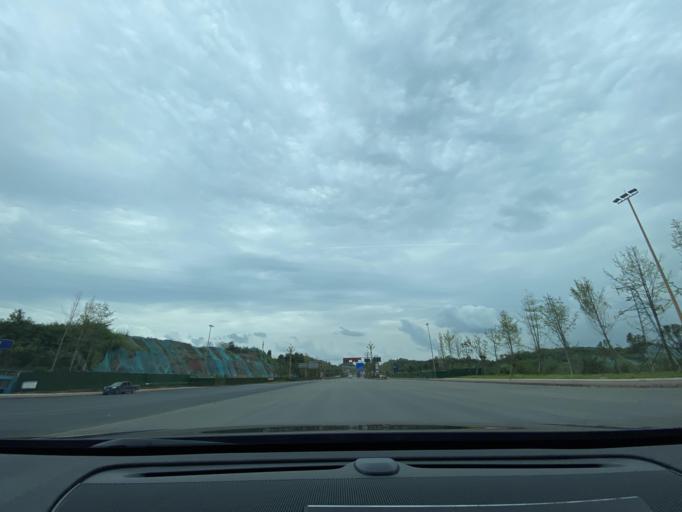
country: CN
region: Sichuan
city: Jiancheng
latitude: 30.4814
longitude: 104.4845
